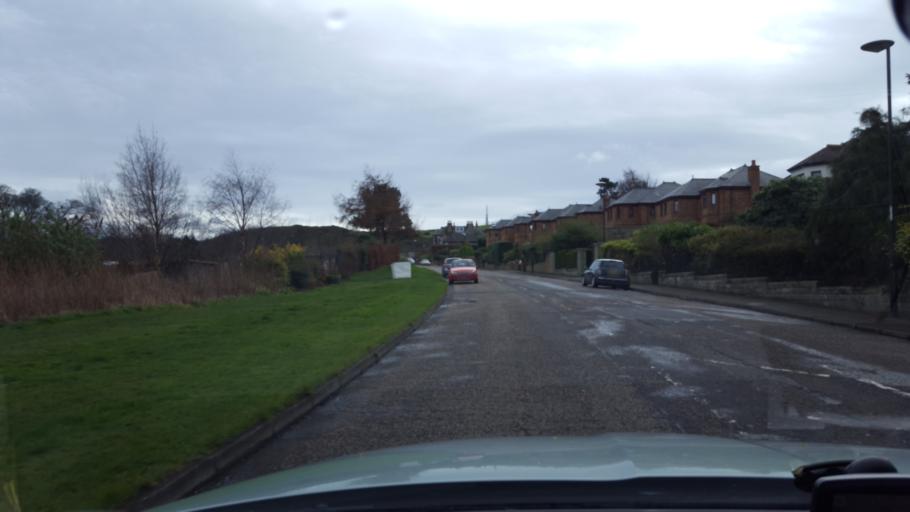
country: GB
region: Scotland
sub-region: Edinburgh
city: Edinburgh
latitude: 55.9232
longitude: -3.2002
